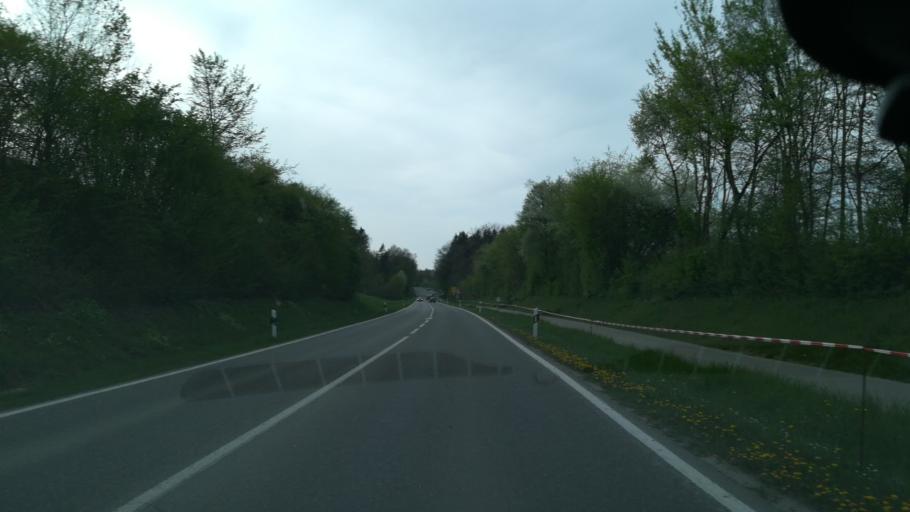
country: DE
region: Baden-Wuerttemberg
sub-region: Freiburg Region
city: Moos
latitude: 47.7561
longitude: 8.9123
